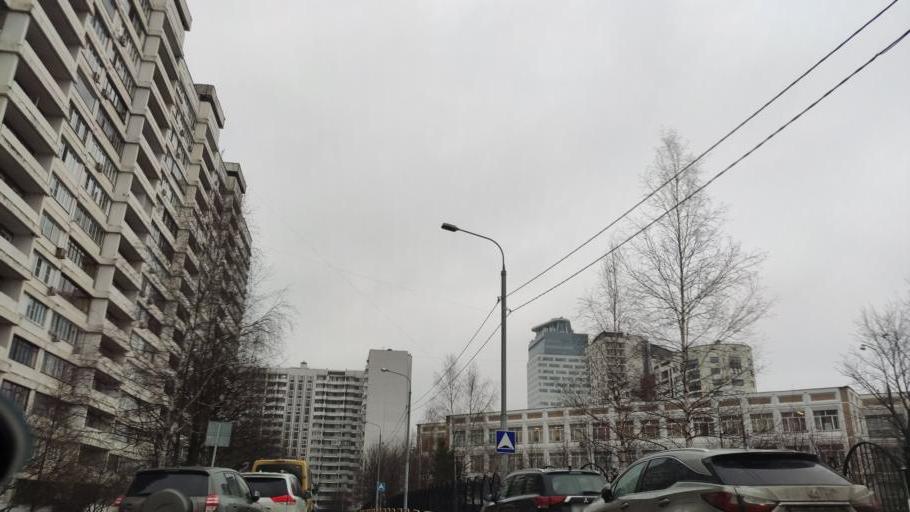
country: RU
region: Moskovskaya
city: Bol'shaya Setun'
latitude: 55.7445
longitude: 37.4295
